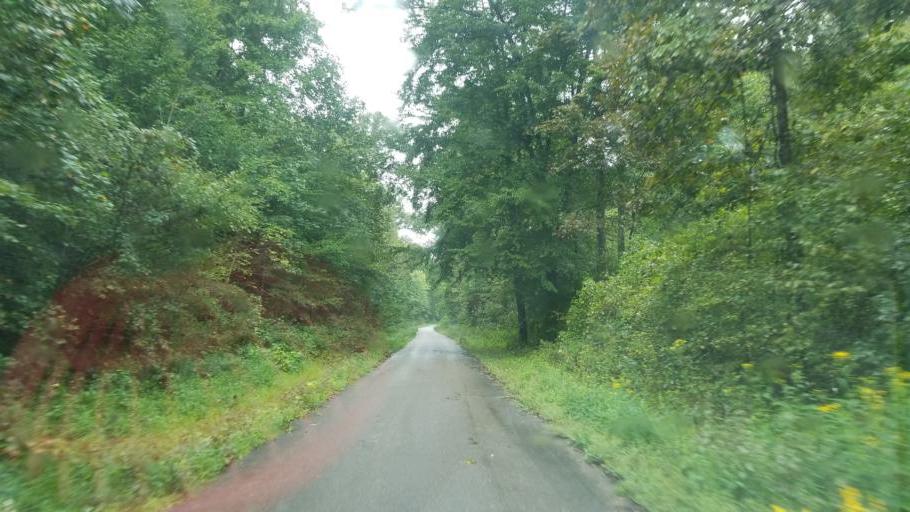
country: US
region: Ohio
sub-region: Scioto County
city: West Portsmouth
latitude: 38.7746
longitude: -83.1504
